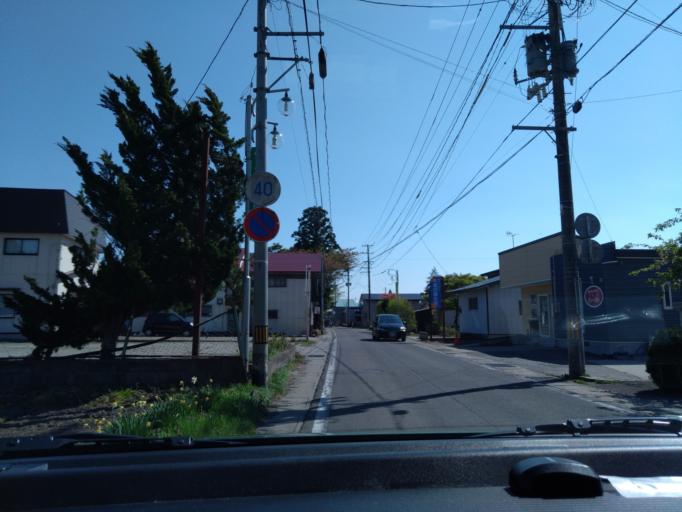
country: JP
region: Akita
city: Kakunodatemachi
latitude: 39.5037
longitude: 140.5951
